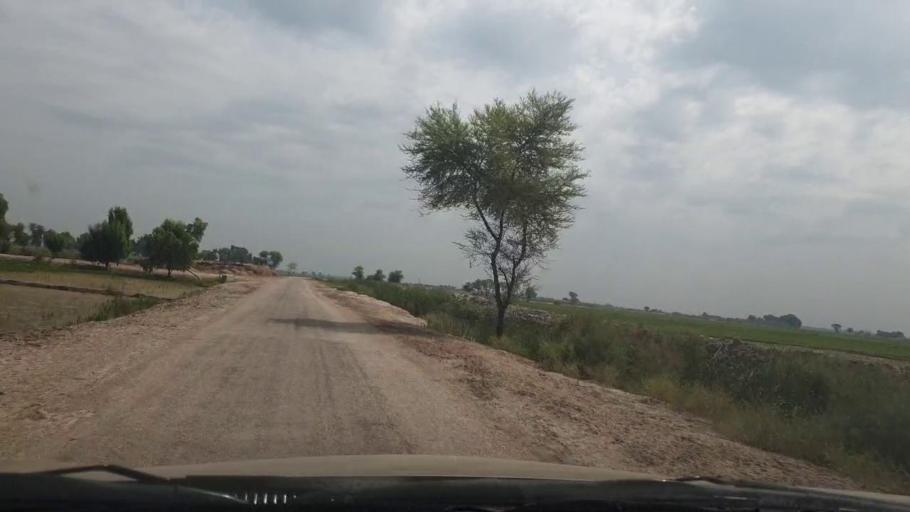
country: PK
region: Sindh
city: Ratodero
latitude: 27.6961
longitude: 68.2121
